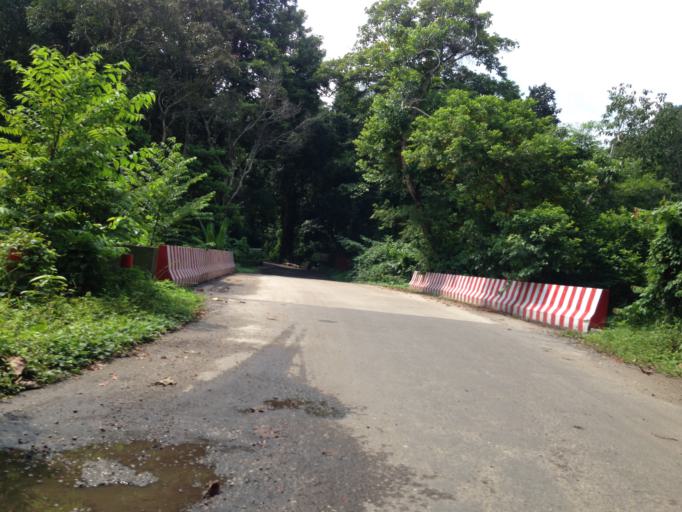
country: IN
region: Tripura
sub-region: Dhalai
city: Kamalpur
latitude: 24.3135
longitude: 91.7742
